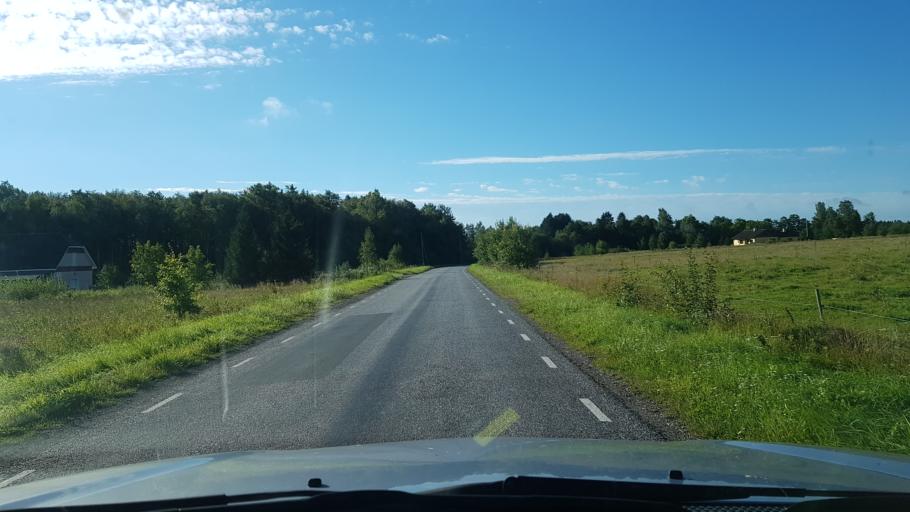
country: EE
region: Harju
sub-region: Rae vald
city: Vaida
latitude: 59.3060
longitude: 24.9260
